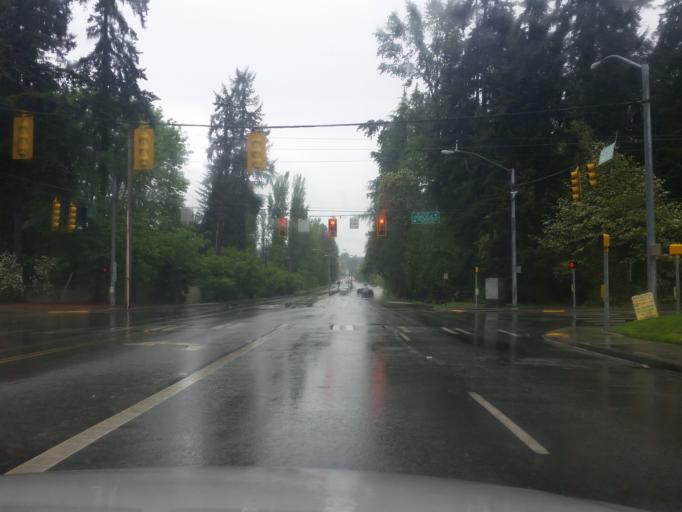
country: US
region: Washington
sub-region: King County
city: Kenmore
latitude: 47.7513
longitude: -122.2499
